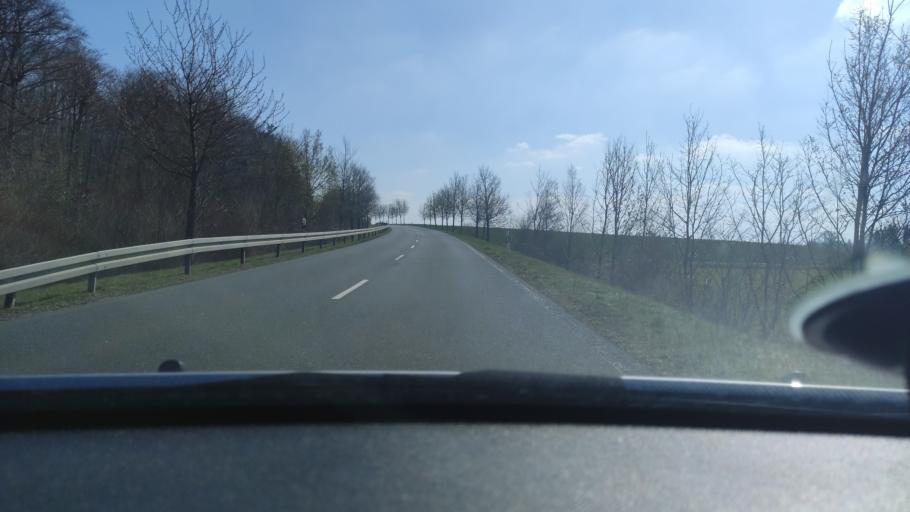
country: DE
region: Baden-Wuerttemberg
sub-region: Regierungsbezirk Stuttgart
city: Assamstadt
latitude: 49.4511
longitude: 9.6664
